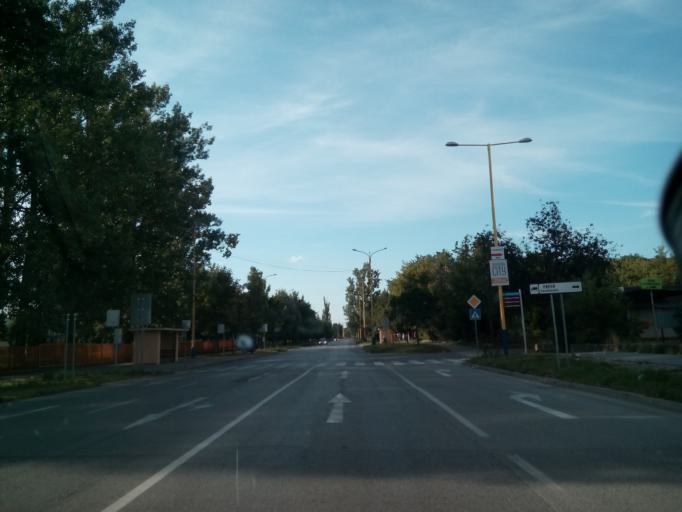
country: SK
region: Kosicky
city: Kosice
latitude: 48.6296
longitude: 21.1727
